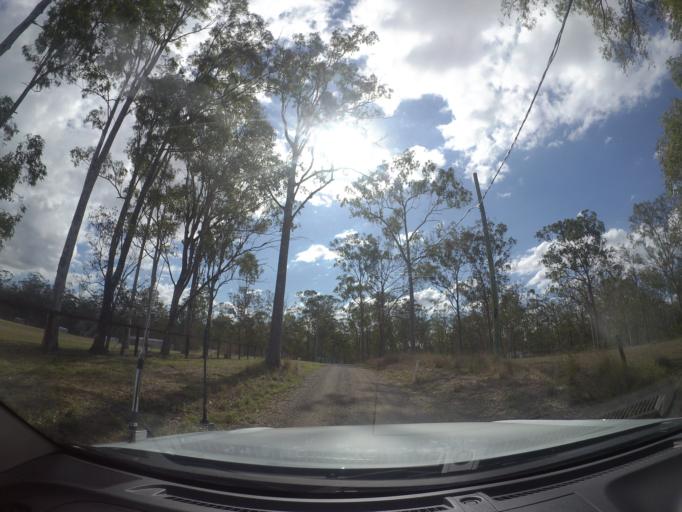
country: AU
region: Queensland
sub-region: Logan
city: North Maclean
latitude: -27.8074
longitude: 152.9950
